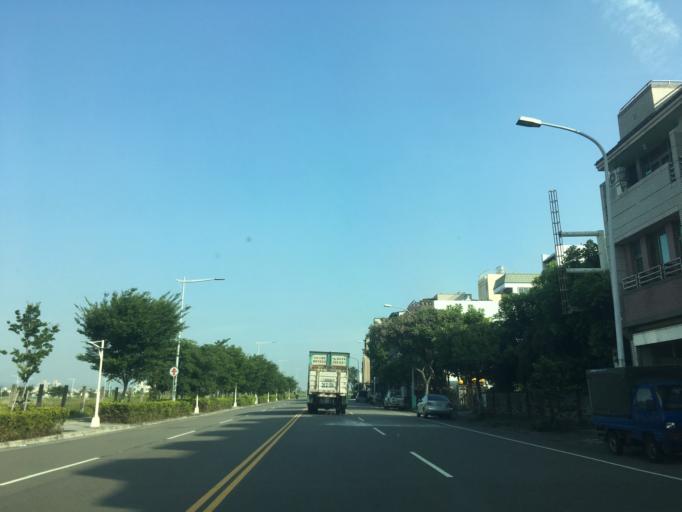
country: TW
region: Taiwan
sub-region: Taichung City
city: Taichung
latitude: 24.1908
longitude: 120.6783
